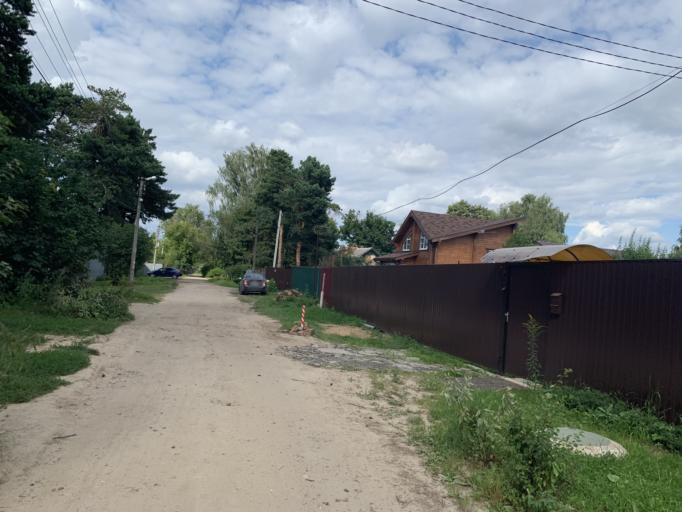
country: RU
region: Moskovskaya
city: Mamontovka
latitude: 55.9862
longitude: 37.8034
